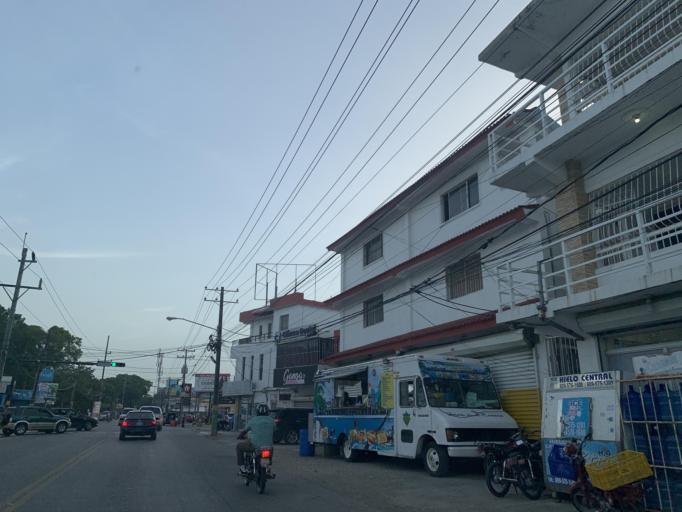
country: DO
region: Puerto Plata
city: Cabarete
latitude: 19.7638
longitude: -70.5133
